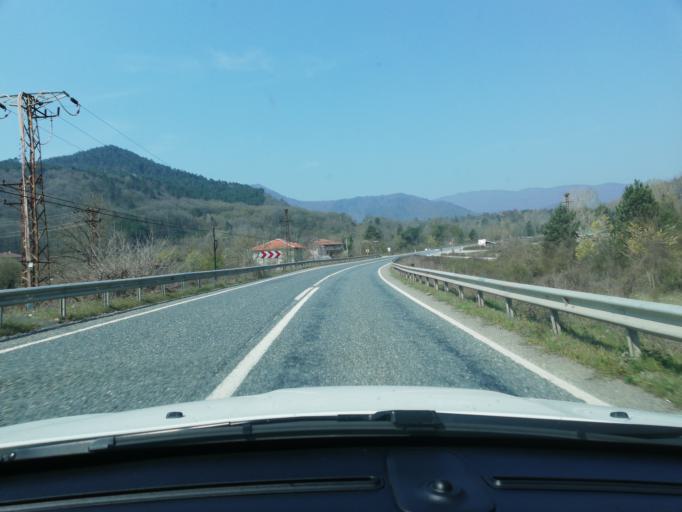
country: TR
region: Zonguldak
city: Gokcebey
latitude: 41.2315
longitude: 32.1983
